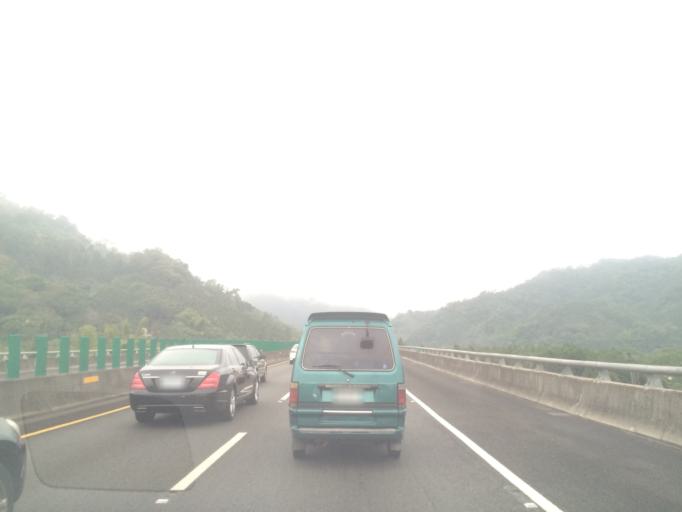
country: TW
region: Taiwan
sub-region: Nantou
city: Puli
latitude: 23.9885
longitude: 120.8568
